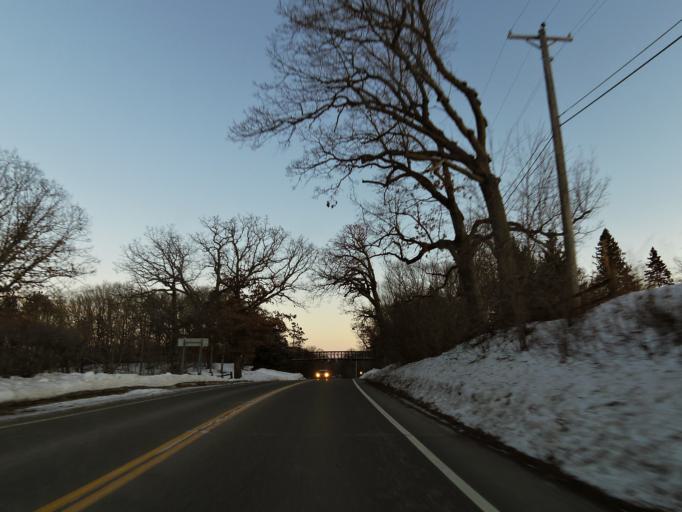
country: US
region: Minnesota
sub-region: Washington County
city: Dellwood
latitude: 45.0936
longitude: -92.9682
